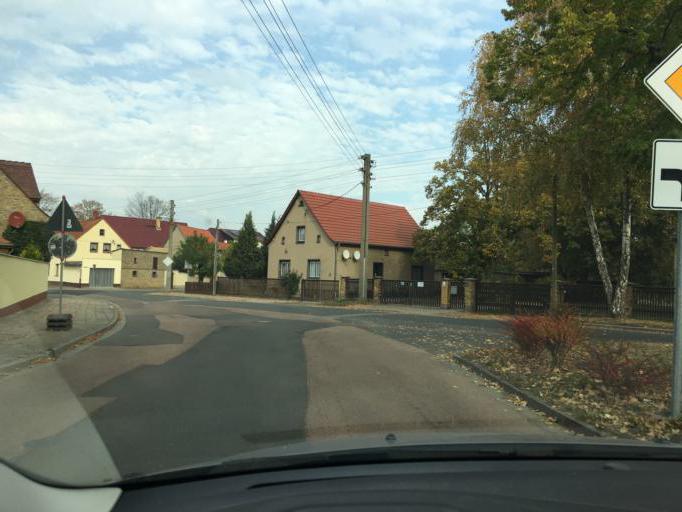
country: DE
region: Saxony
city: Zwochau
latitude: 51.4636
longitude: 12.2712
